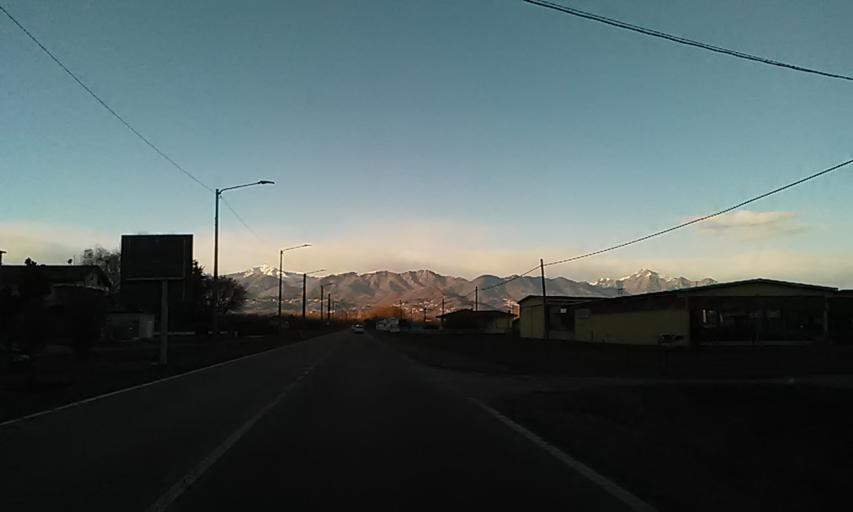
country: IT
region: Piedmont
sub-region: Provincia di Biella
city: Cossato
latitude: 45.5349
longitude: 8.1868
